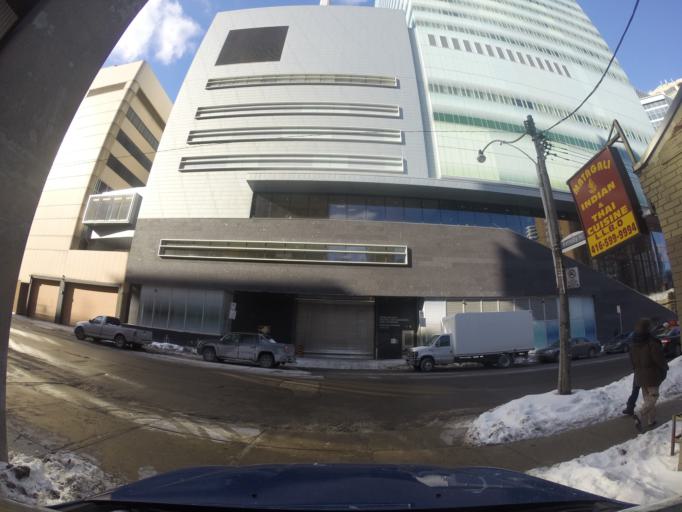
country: CA
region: Ontario
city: Toronto
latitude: 43.6569
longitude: -79.3850
